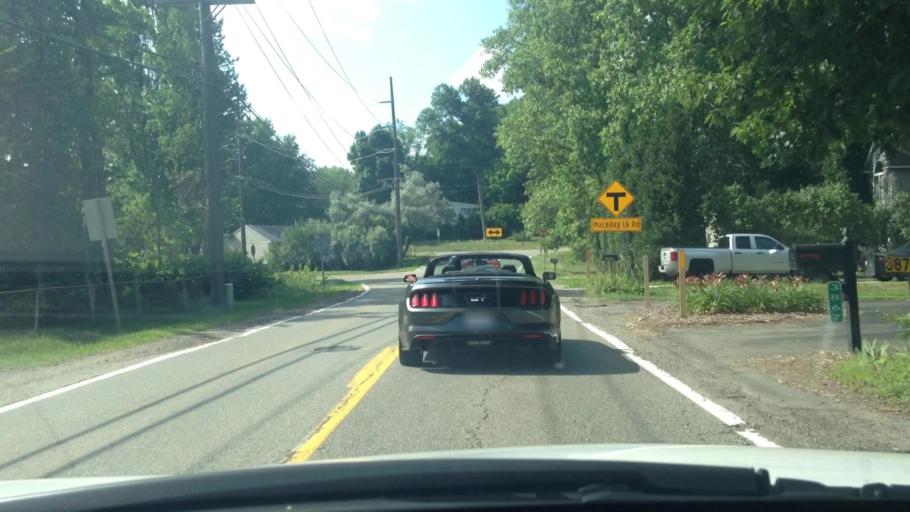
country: US
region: Michigan
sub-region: Oakland County
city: Waterford
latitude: 42.6935
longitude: -83.4414
